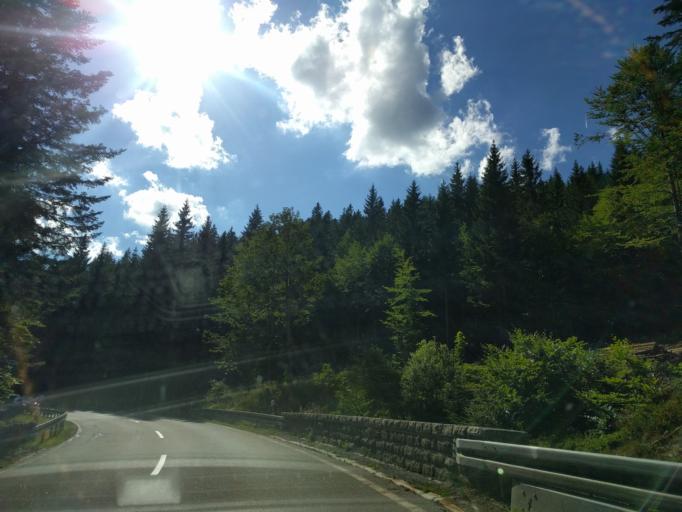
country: DE
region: Bavaria
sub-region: Lower Bavaria
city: Bodenmais
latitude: 49.0706
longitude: 13.1397
